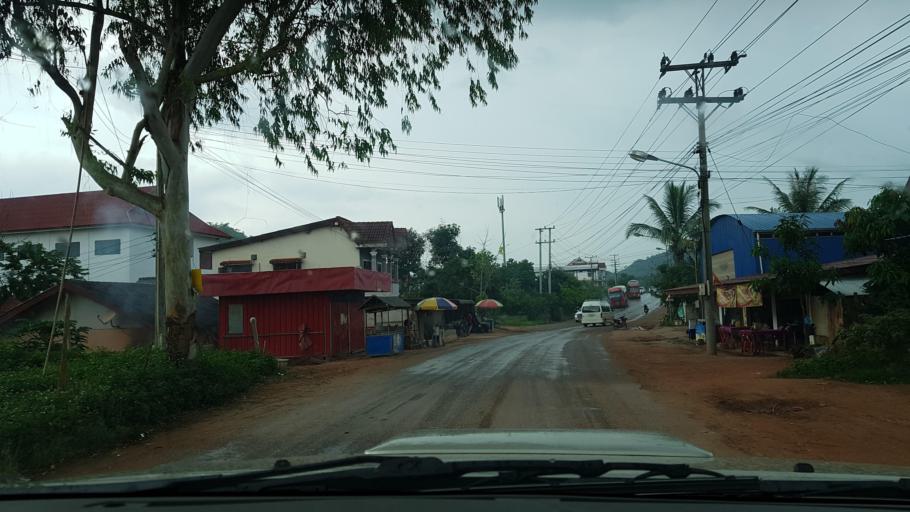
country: LA
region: Oudomxai
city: Muang Xay
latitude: 20.6426
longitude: 101.9734
